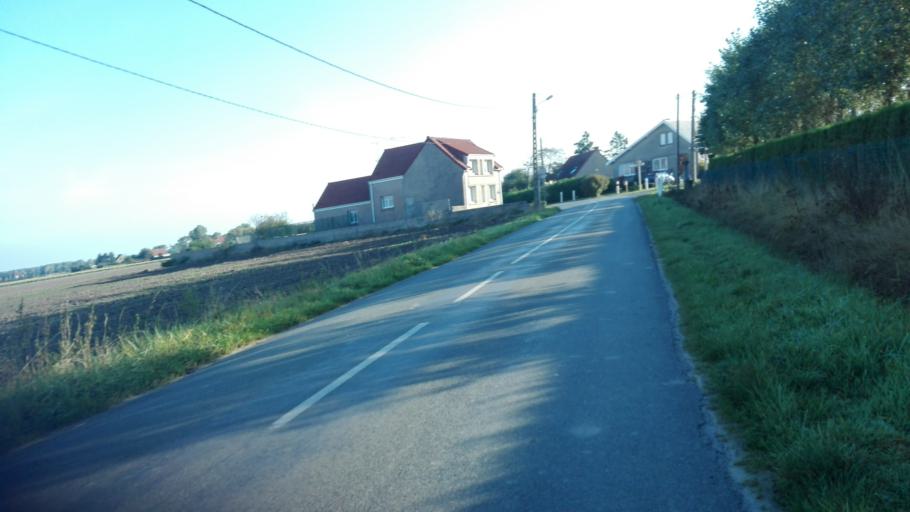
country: FR
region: Nord-Pas-de-Calais
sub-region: Departement du Nord
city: Zuydcoote
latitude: 51.0482
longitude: 2.4937
